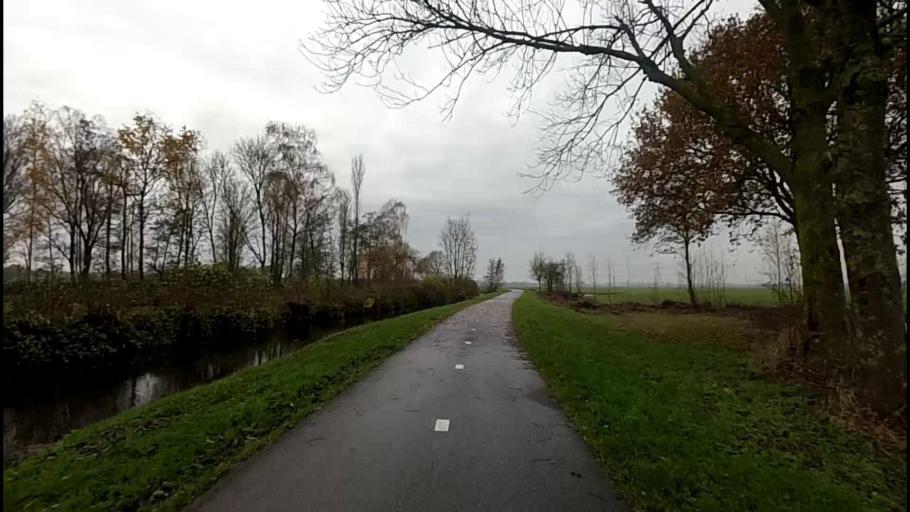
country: NL
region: South Holland
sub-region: Molenwaard
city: Nieuw-Lekkerland
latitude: 51.9173
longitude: 4.6522
